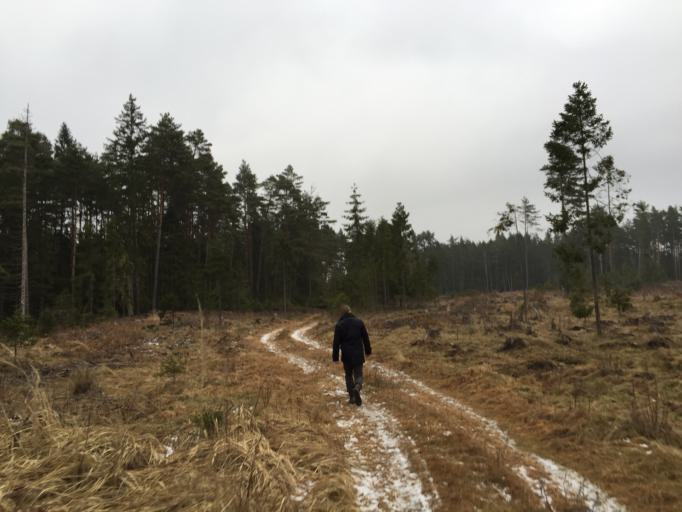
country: EE
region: Saare
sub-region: Kuressaare linn
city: Kuressaare
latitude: 58.4984
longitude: 22.3769
